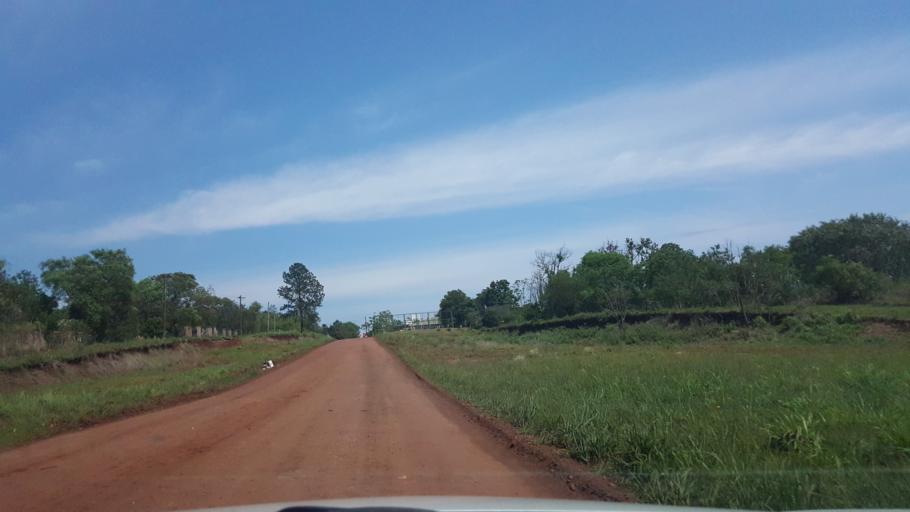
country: AR
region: Misiones
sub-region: Departamento de Apostoles
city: San Jose
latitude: -27.7527
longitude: -55.7874
